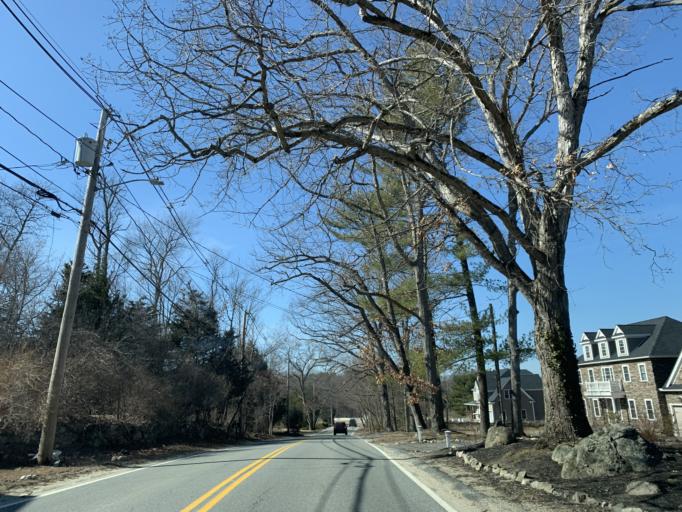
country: US
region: Massachusetts
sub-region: Norfolk County
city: Sharon
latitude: 42.1474
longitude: -71.1853
